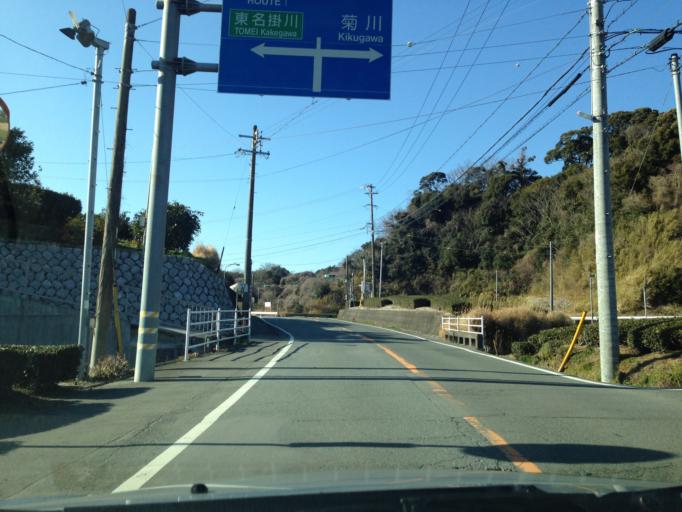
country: JP
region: Shizuoka
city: Kakegawa
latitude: 34.7590
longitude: 138.0466
